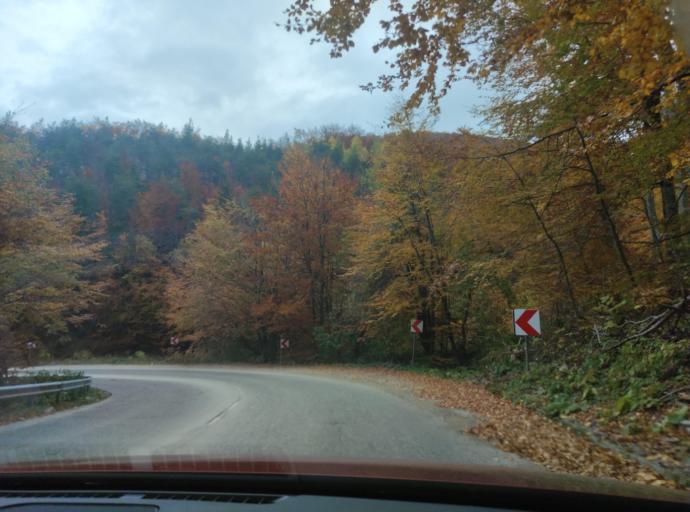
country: BG
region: Montana
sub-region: Obshtina Berkovitsa
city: Berkovitsa
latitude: 43.1361
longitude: 23.1429
